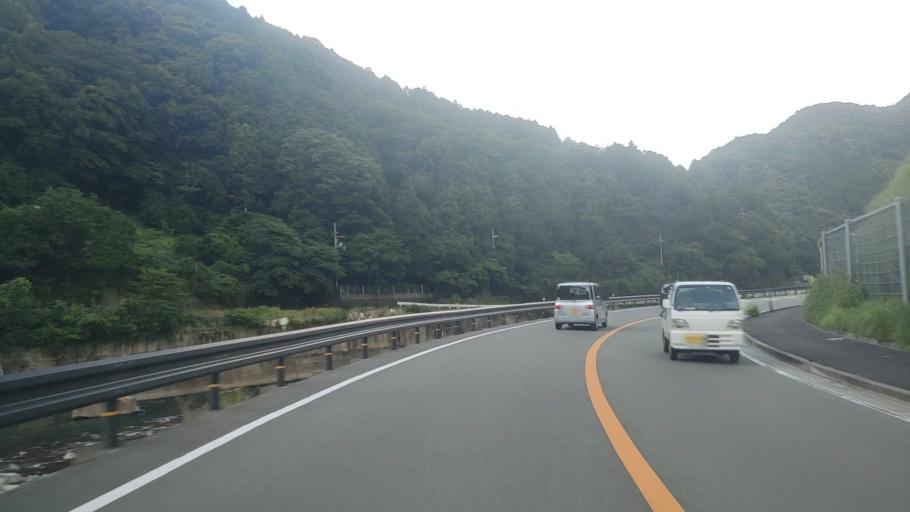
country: JP
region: Wakayama
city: Tanabe
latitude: 33.7734
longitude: 135.5010
